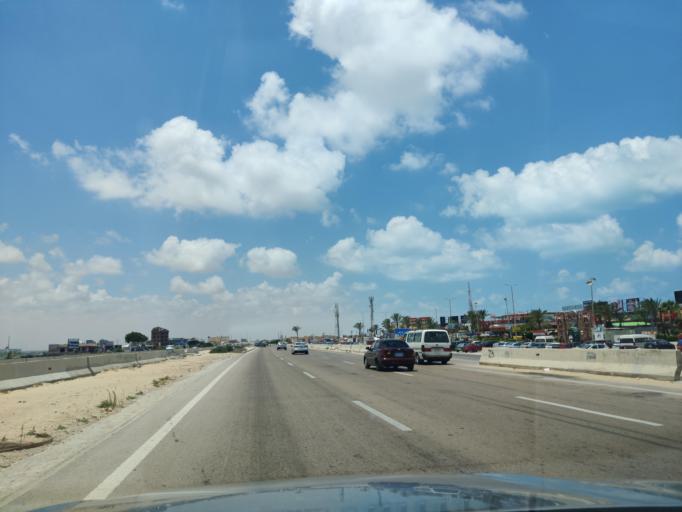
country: EG
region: Muhafazat Matruh
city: Al `Alamayn
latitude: 30.8220
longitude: 29.1752
